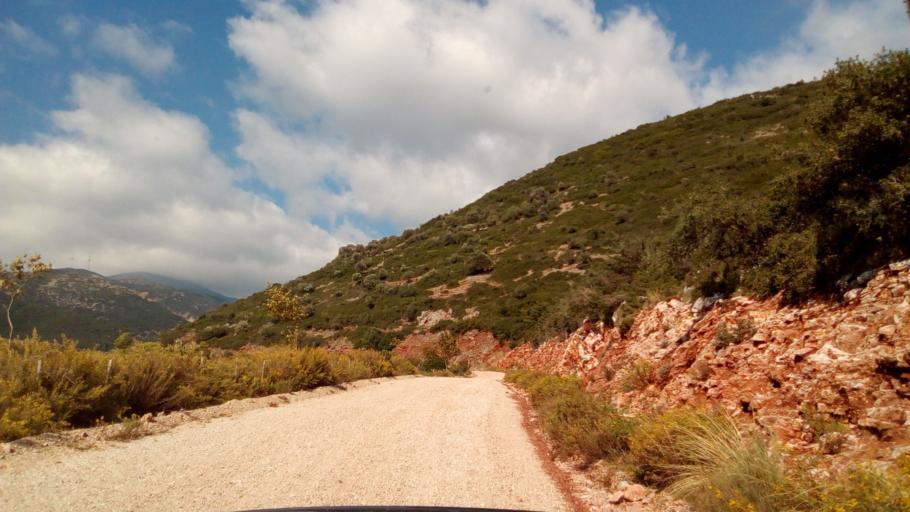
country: GR
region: West Greece
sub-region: Nomos Aitolias kai Akarnanias
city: Nafpaktos
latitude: 38.4141
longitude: 21.8466
